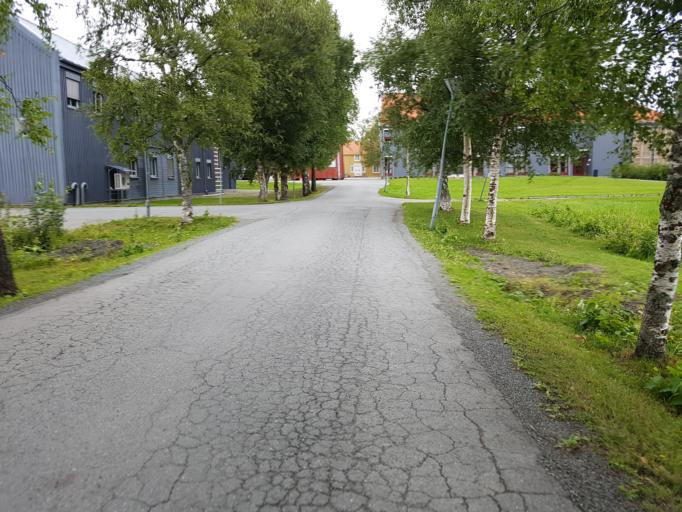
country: NO
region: Sor-Trondelag
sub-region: Trondheim
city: Trondheim
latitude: 63.4076
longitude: 10.4653
